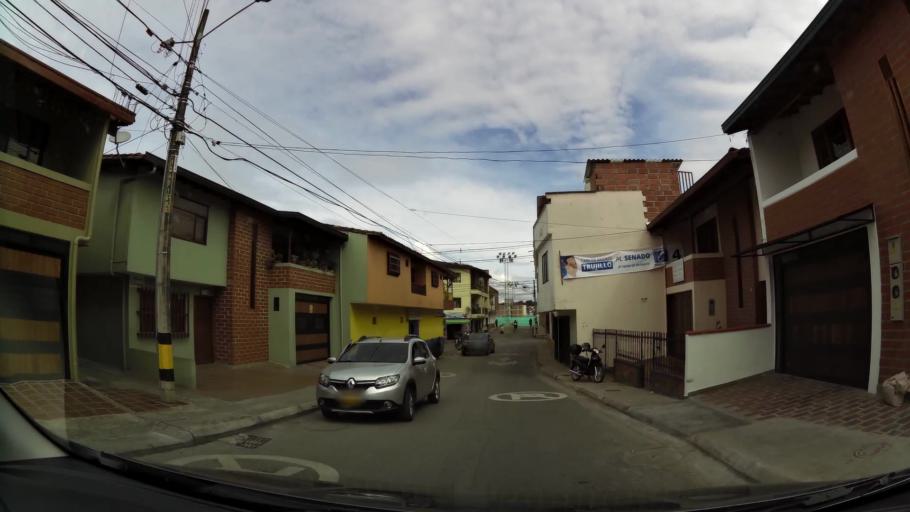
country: CO
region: Antioquia
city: Rionegro
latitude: 6.1588
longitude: -75.3731
